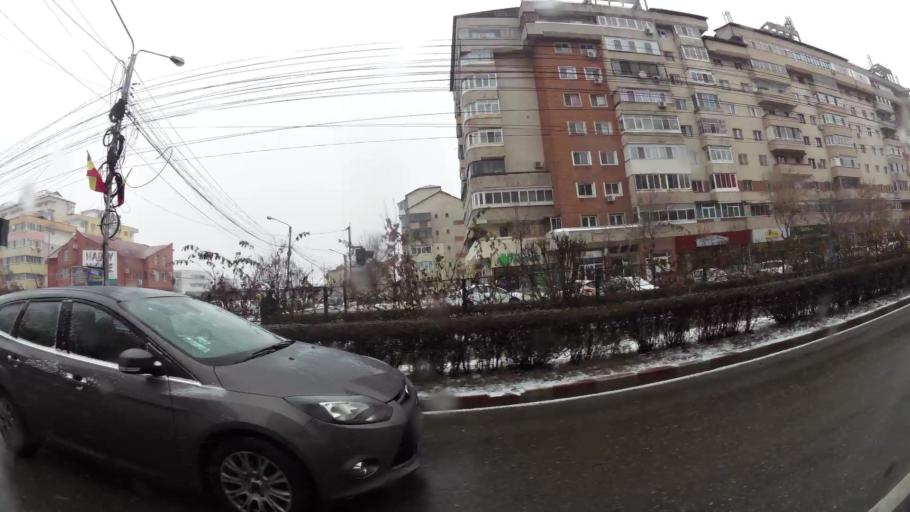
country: RO
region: Dambovita
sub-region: Municipiul Targoviste
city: Targoviste
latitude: 44.9195
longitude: 25.4776
